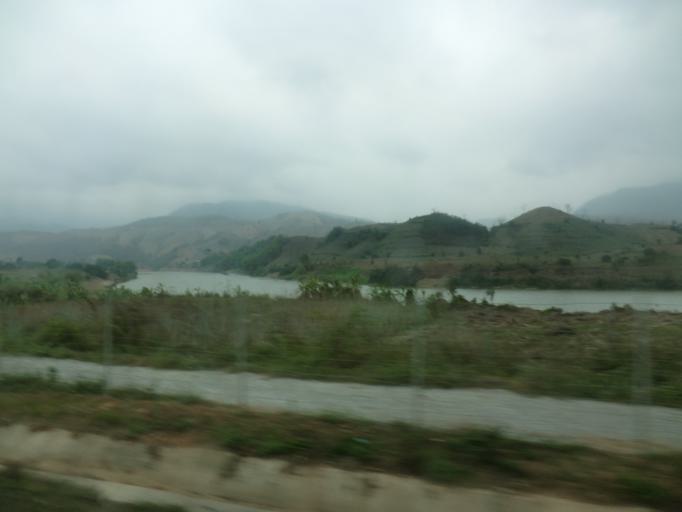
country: VN
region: Yen Bai
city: Thi Tran Yen The
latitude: 21.9841
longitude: 104.5561
